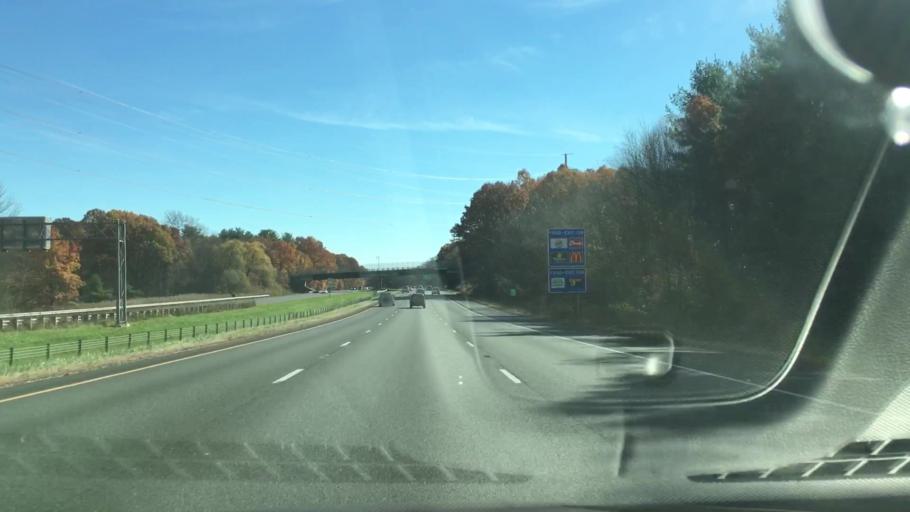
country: US
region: Massachusetts
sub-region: Hampden County
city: Chicopee
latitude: 42.1452
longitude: -72.6415
